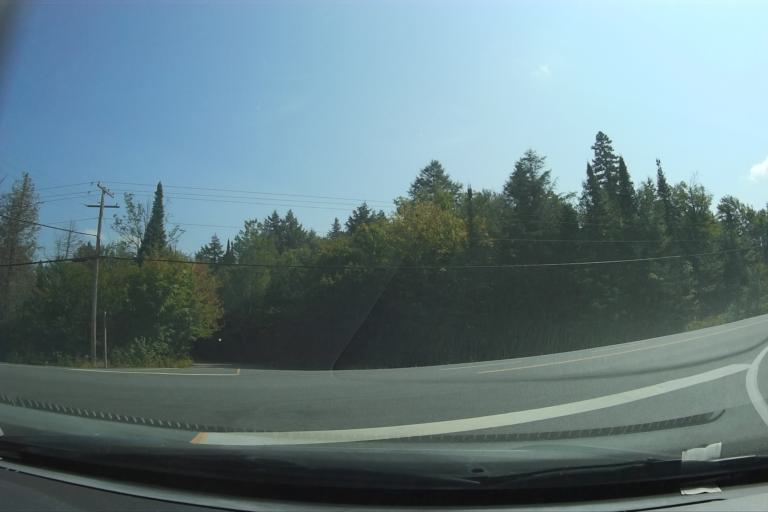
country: CA
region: Ontario
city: Huntsville
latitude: 45.5326
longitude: -78.7042
